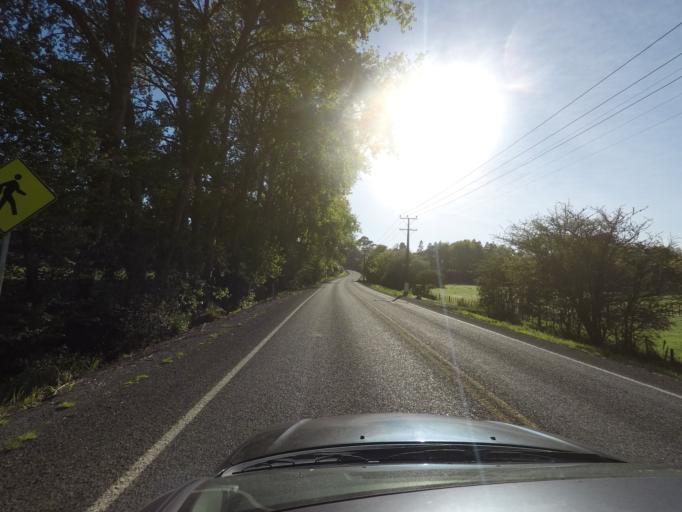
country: NZ
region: Auckland
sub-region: Auckland
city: Red Hill
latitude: -36.9967
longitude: 174.9797
